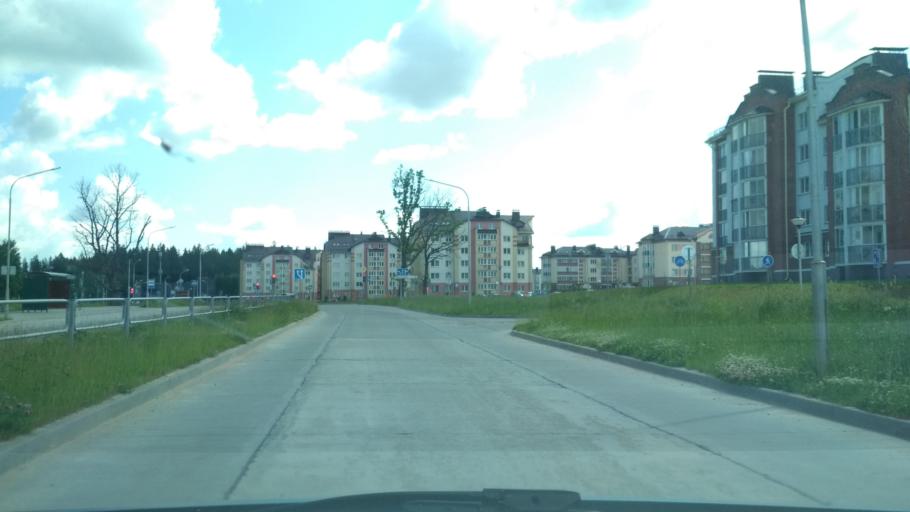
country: BY
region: Grodnenskaya
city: Astravyets
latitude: 54.6002
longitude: 25.9698
